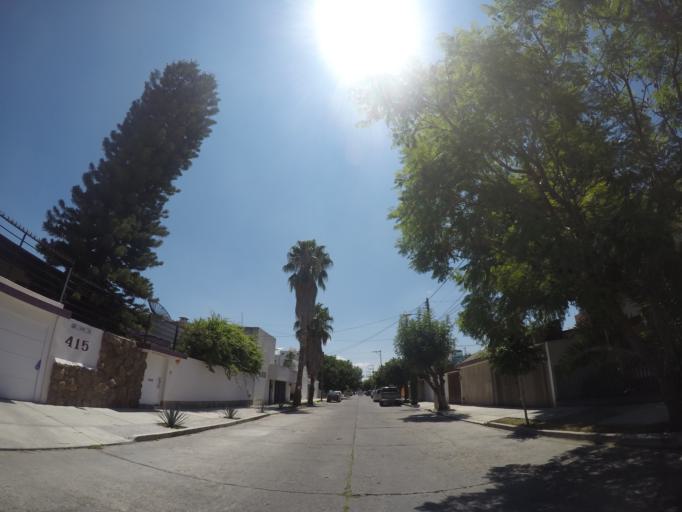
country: MX
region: San Luis Potosi
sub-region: San Luis Potosi
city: San Luis Potosi
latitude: 22.1466
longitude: -101.0058
